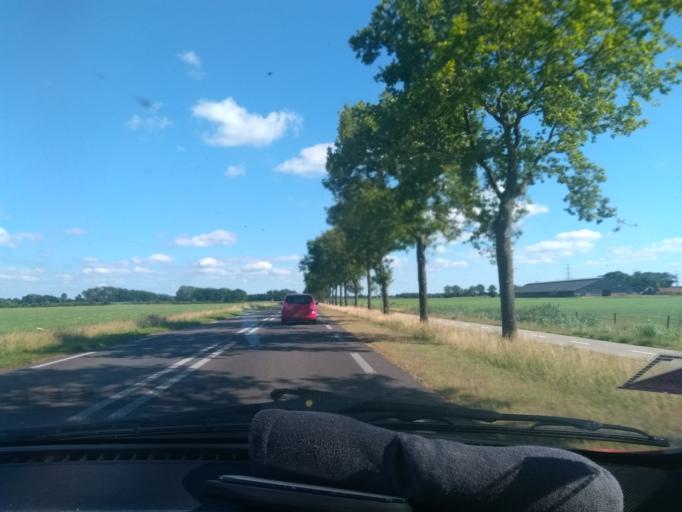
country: NL
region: Drenthe
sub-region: Gemeente Tynaarlo
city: Vries
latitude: 53.1213
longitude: 6.5063
